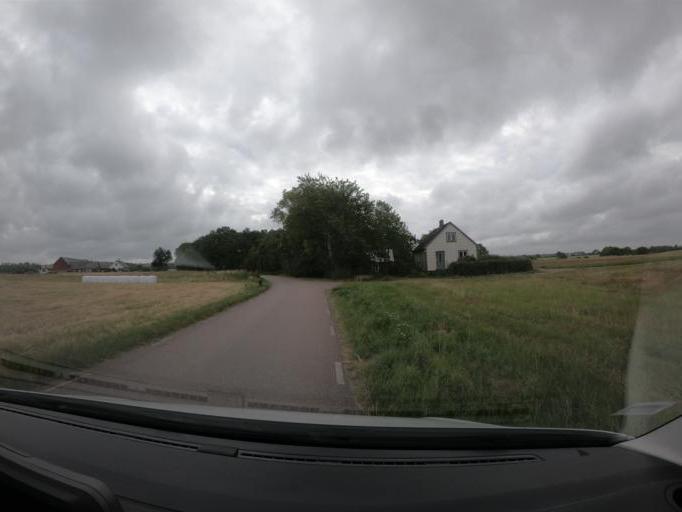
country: SE
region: Skane
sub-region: Angelholms Kommun
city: Vejbystrand
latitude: 56.3538
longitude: 12.7542
